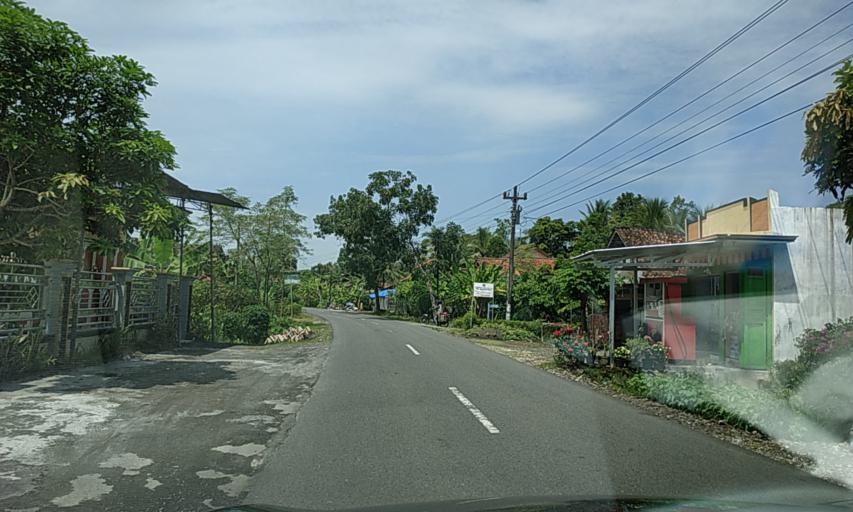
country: ID
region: Central Java
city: Kedungbulu
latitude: -7.5298
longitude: 108.7822
